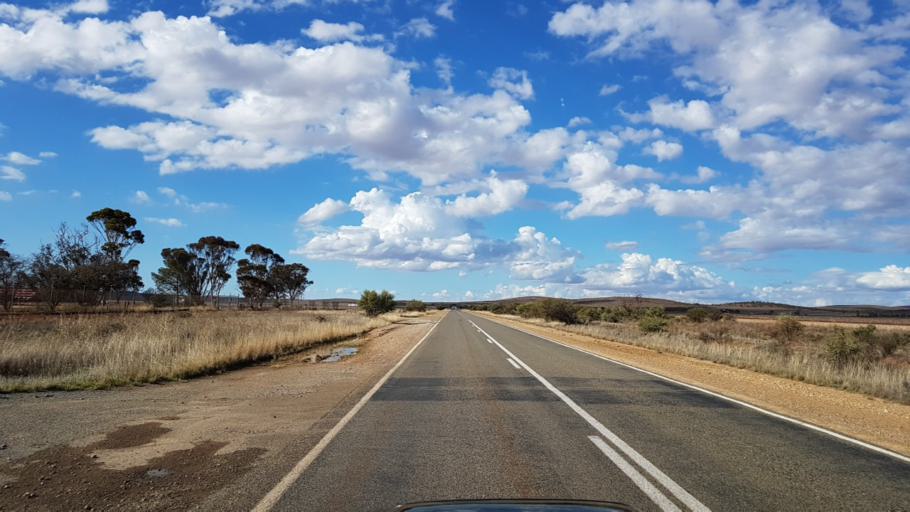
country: AU
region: South Australia
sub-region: Peterborough
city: Peterborough
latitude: -32.9685
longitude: 138.8690
